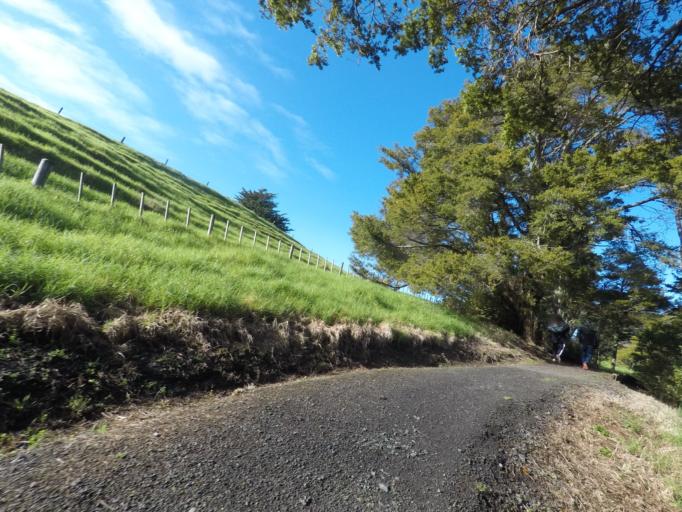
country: NZ
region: Auckland
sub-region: Auckland
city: Warkworth
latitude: -36.4291
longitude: 174.7185
